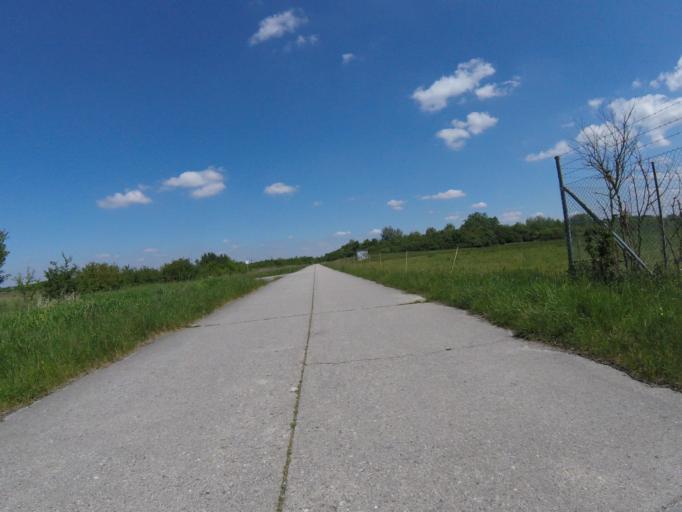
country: DE
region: Bavaria
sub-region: Upper Bavaria
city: Neubiberg
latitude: 48.0690
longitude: 11.6431
